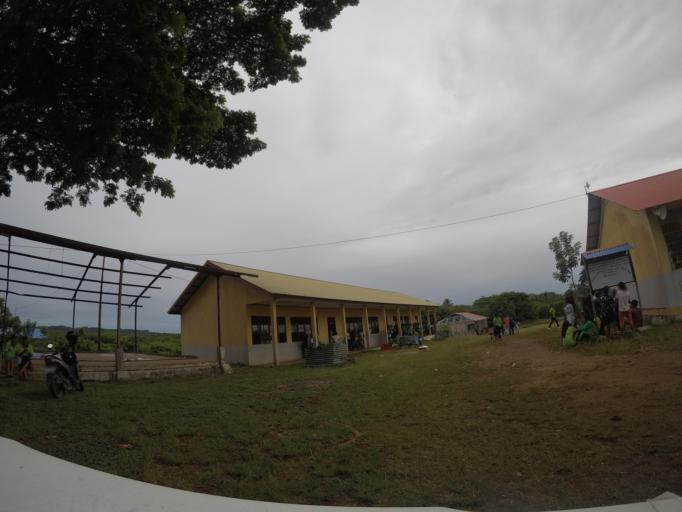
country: TL
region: Lautem
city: Lospalos
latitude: -8.5356
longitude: 126.9992
